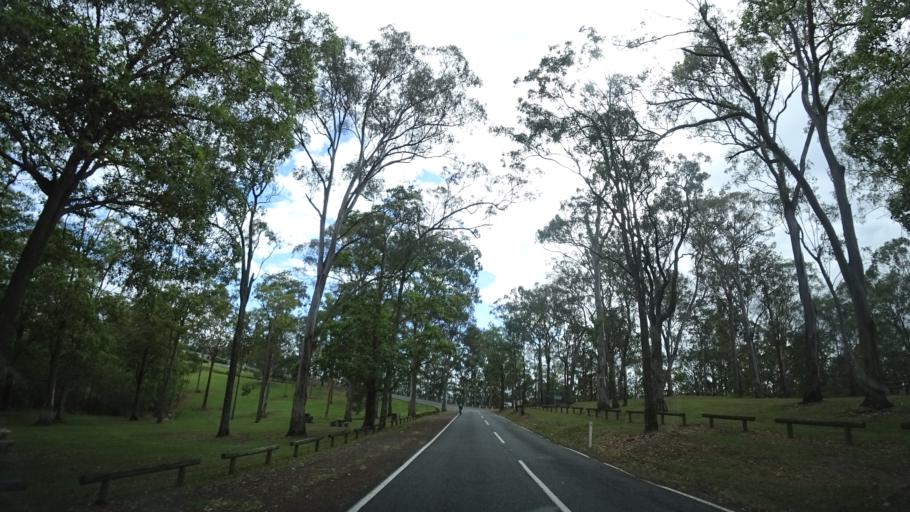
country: AU
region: Queensland
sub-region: Brisbane
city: Kenmore Hills
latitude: -27.4694
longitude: 152.9422
